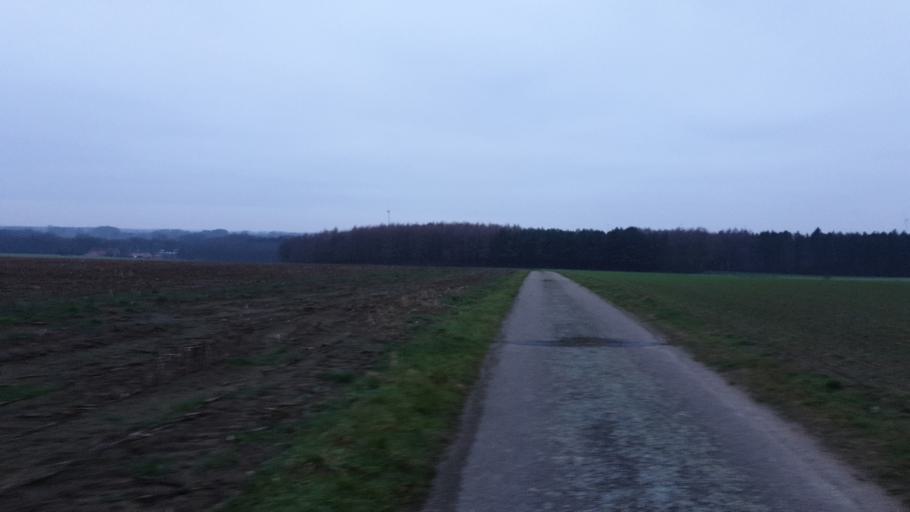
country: DE
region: North Rhine-Westphalia
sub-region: Regierungsbezirk Munster
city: Klein Reken
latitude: 51.7721
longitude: 7.0493
